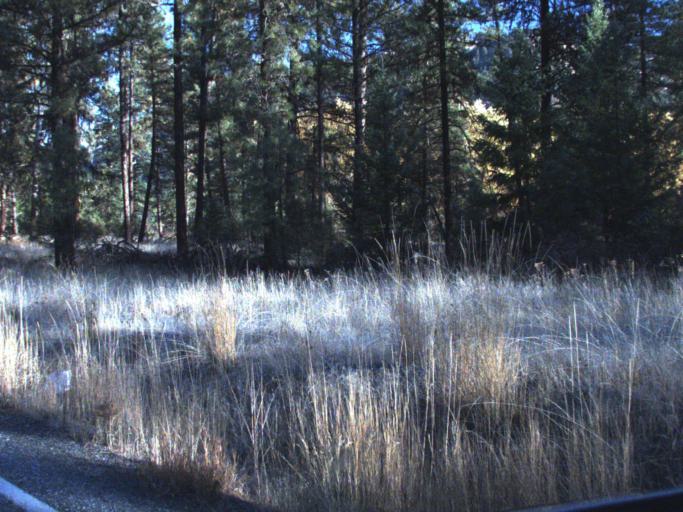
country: US
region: Washington
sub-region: Ferry County
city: Republic
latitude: 48.3230
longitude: -118.7432
